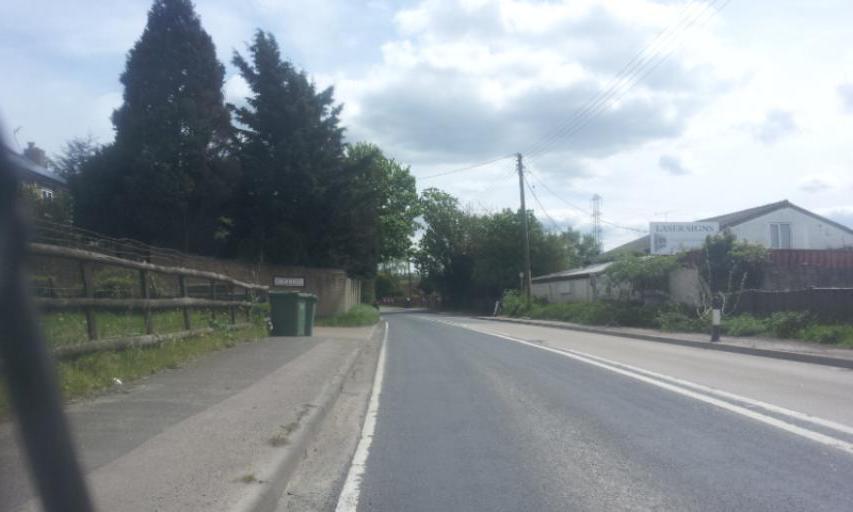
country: GB
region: England
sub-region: Kent
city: Longfield
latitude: 51.4061
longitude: 0.2821
